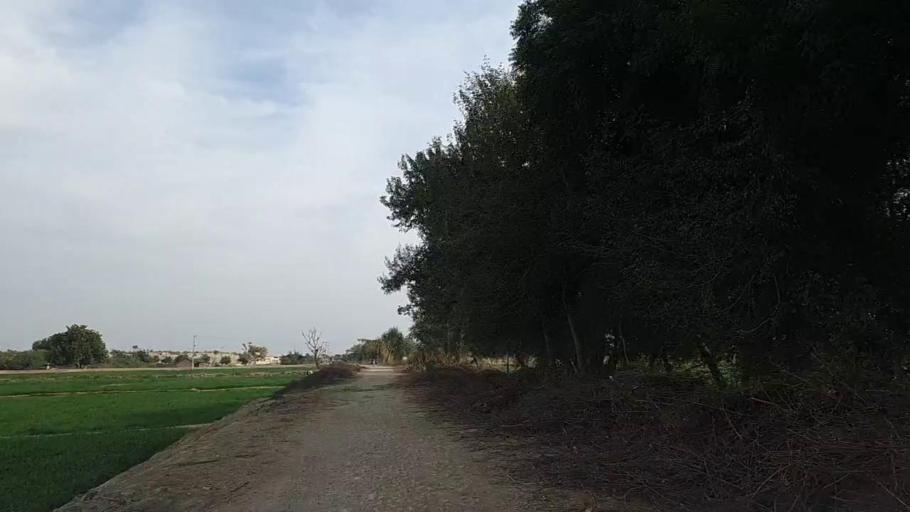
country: PK
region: Sindh
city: Jam Sahib
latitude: 26.4357
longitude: 68.6337
